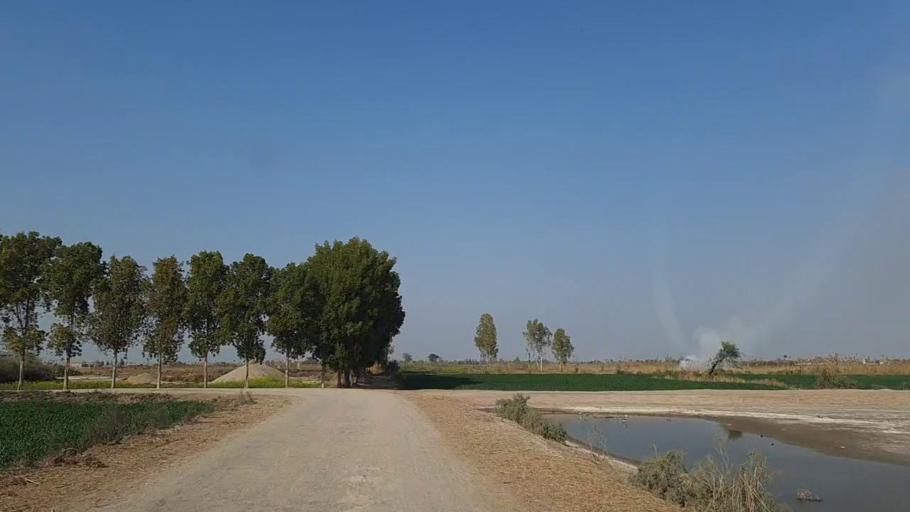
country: PK
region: Sindh
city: Daur
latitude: 26.4708
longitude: 68.3047
